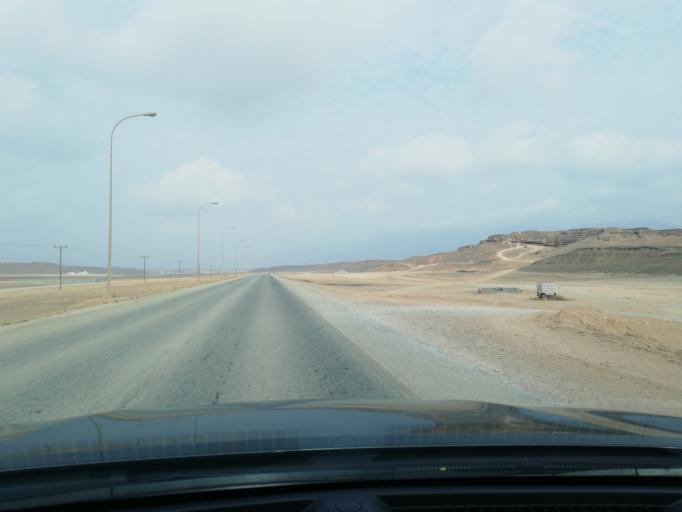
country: OM
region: Zufar
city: Salalah
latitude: 16.9579
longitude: 53.9017
